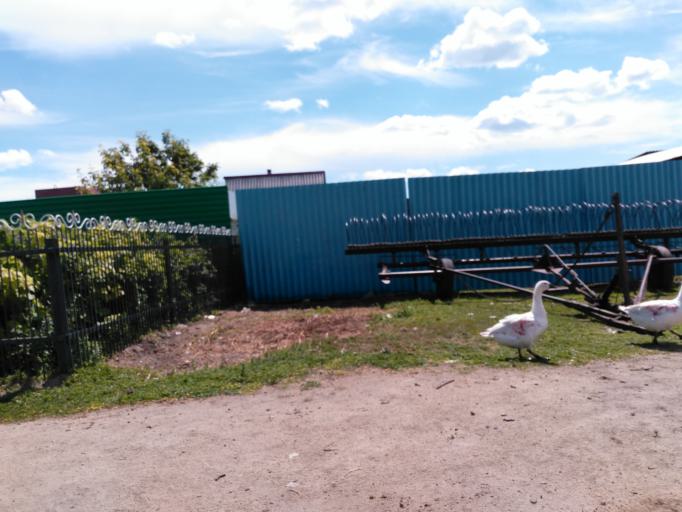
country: RU
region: Bashkortostan
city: Akhunovo
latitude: 54.2013
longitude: 59.5945
